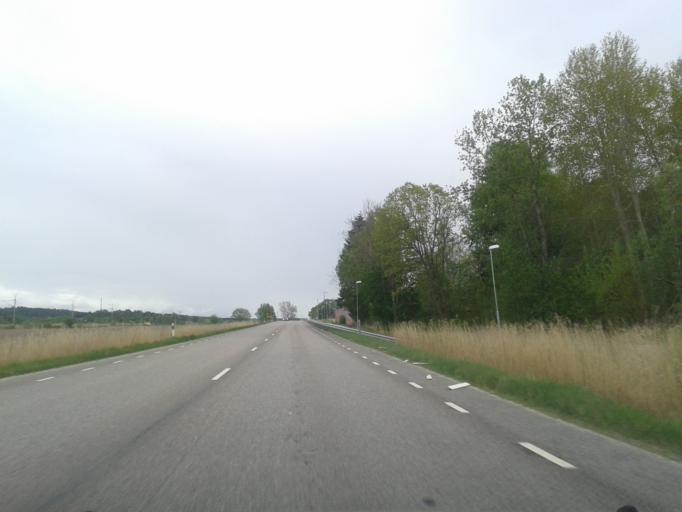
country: SE
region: Vaestra Goetaland
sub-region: Stenungsunds Kommun
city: Stora Hoga
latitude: 57.9947
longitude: 11.8286
